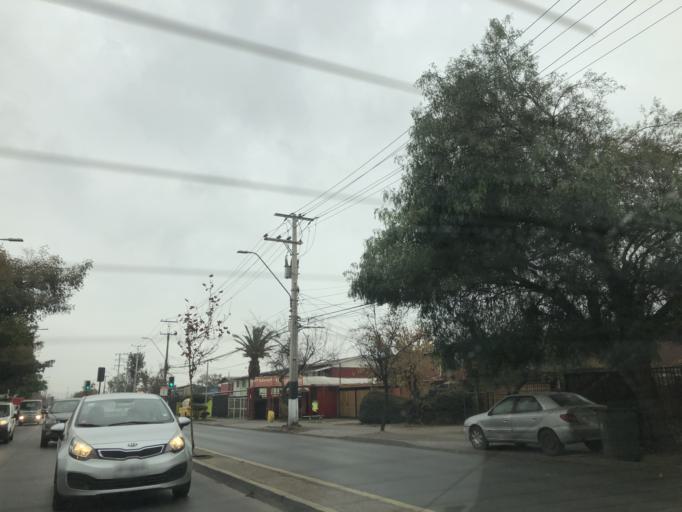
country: CL
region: Santiago Metropolitan
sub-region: Provincia de Santiago
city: La Pintana
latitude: -33.5817
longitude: -70.5997
